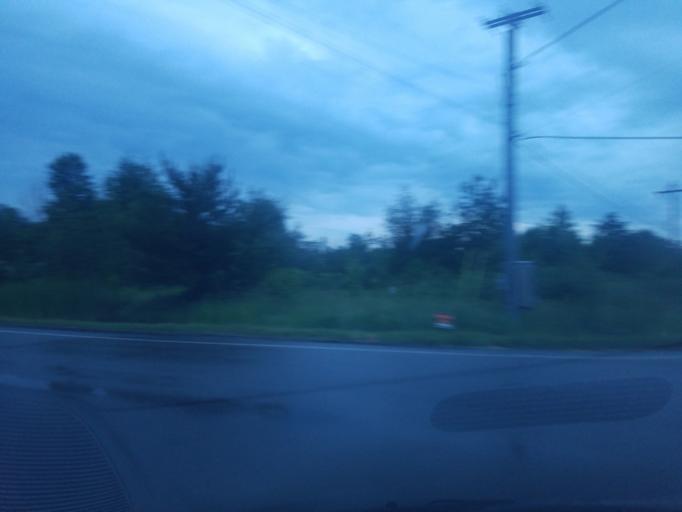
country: US
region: Ohio
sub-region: Mahoning County
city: Canfield
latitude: 40.9882
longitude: -80.7592
